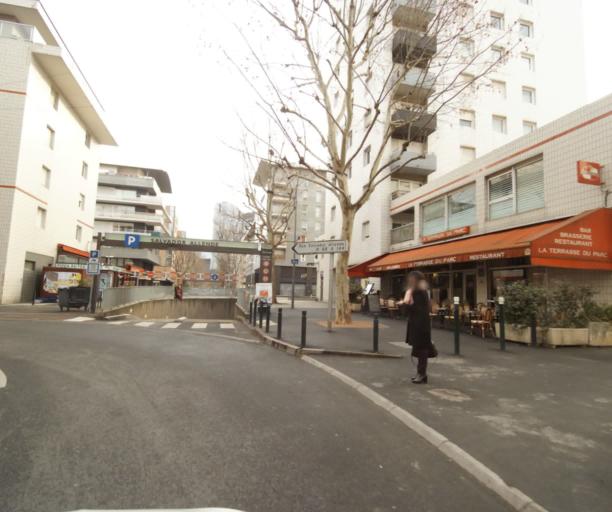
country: FR
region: Ile-de-France
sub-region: Departement des Hauts-de-Seine
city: Nanterre
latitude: 48.8951
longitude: 2.2220
